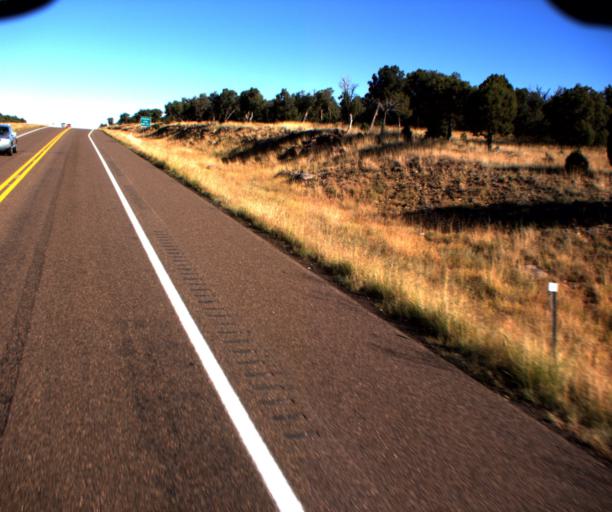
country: US
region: Arizona
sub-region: Navajo County
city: White Mountain Lake
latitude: 34.3297
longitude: -110.0465
